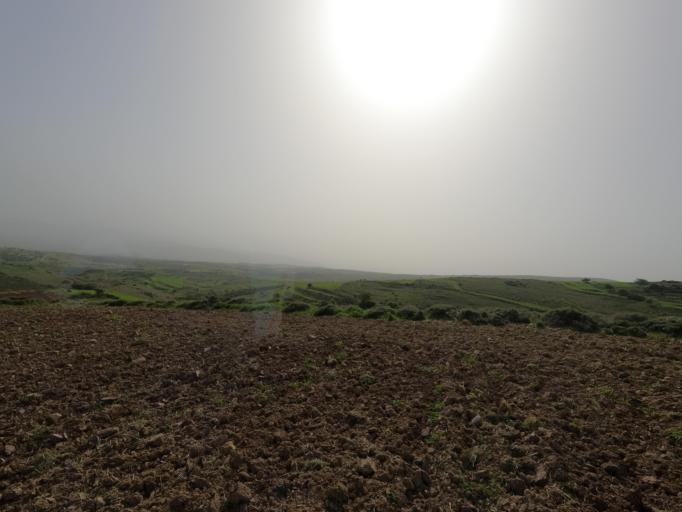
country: CY
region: Pafos
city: Polis
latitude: 35.0038
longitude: 32.3498
